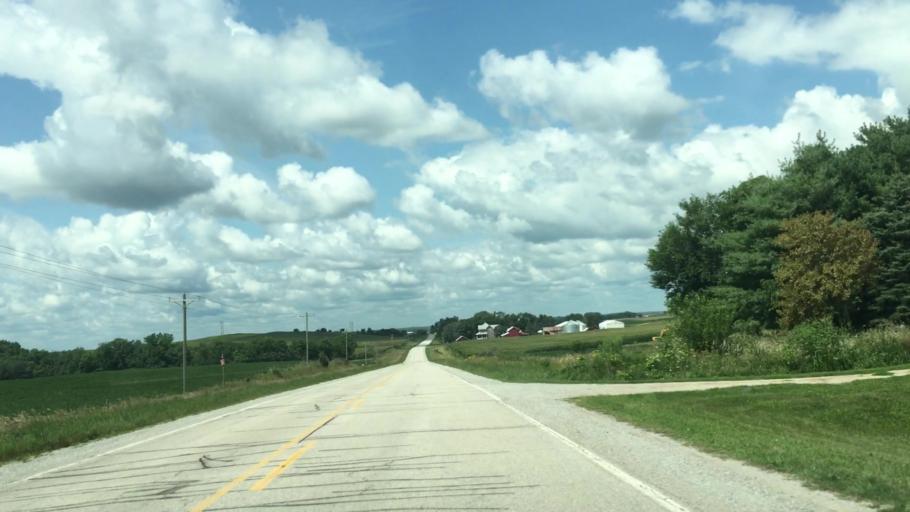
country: US
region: Iowa
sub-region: Johnson County
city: Solon
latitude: 41.8313
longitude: -91.4702
